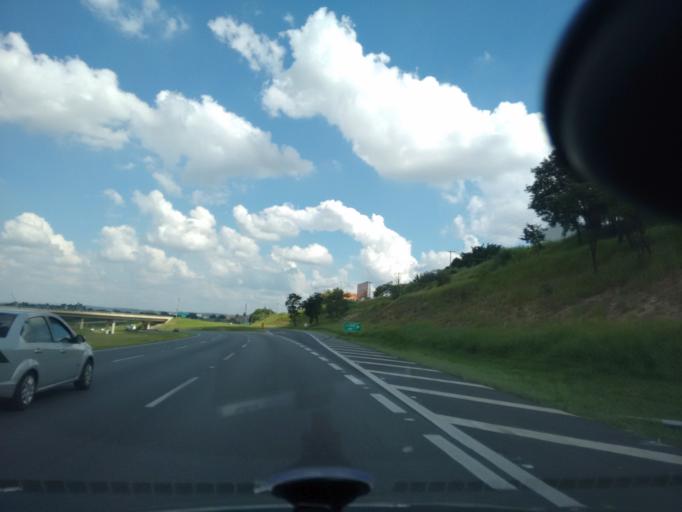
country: BR
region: Sao Paulo
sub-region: Campinas
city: Campinas
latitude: -22.9894
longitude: -47.1116
